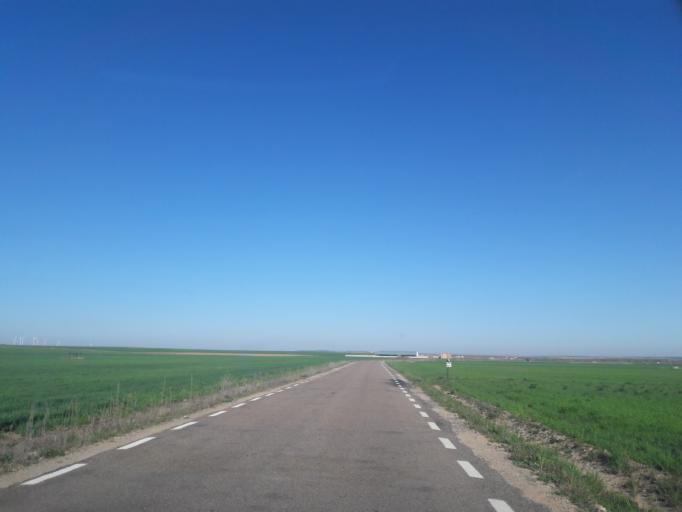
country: ES
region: Castille and Leon
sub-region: Provincia de Salamanca
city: Coca de Alba
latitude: 40.8630
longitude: -5.3686
